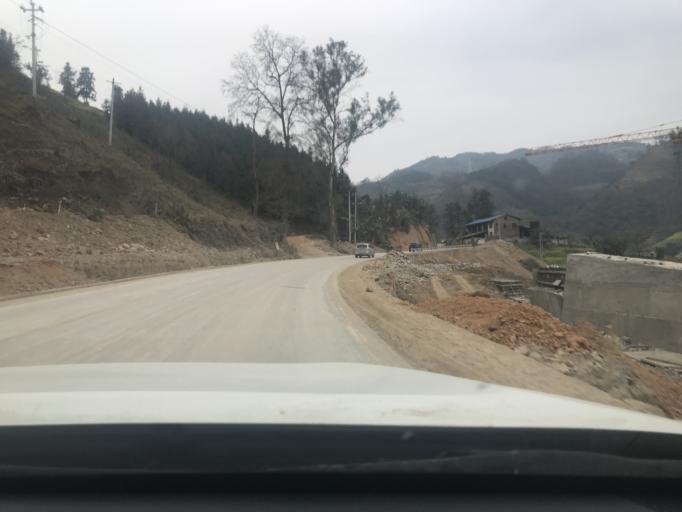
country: CN
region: Guangxi Zhuangzu Zizhiqu
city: Xinzhou
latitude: 25.0091
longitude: 105.8505
